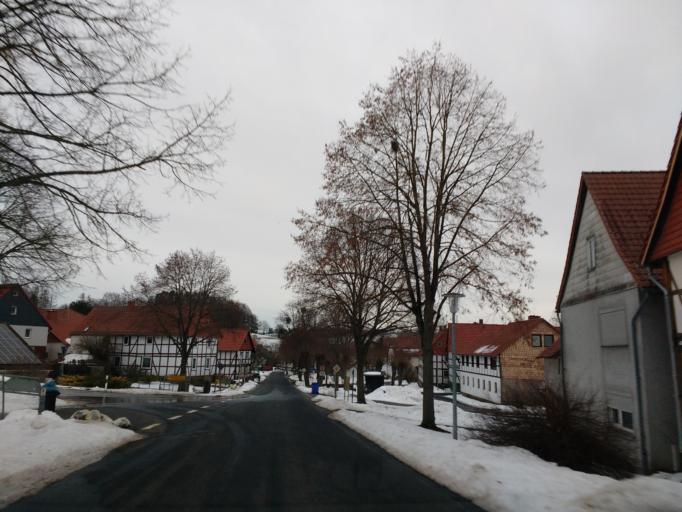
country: DE
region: Thuringia
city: Rustenfelde
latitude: 51.4249
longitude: 9.9804
